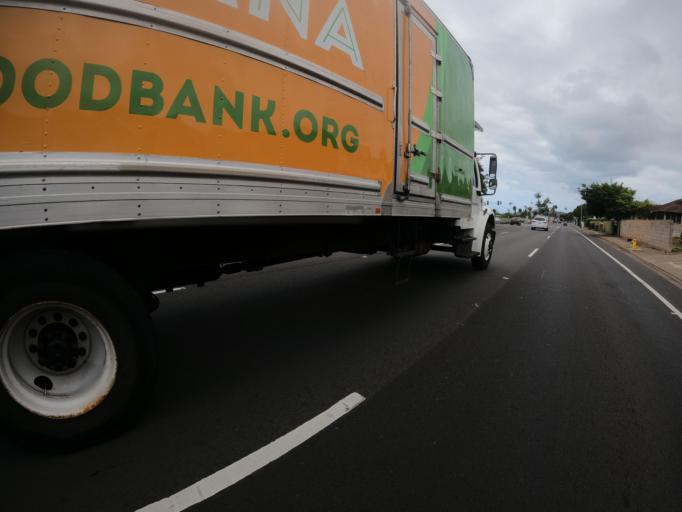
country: US
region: Hawaii
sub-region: Honolulu County
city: Waimanalo
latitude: 21.2780
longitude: -157.7565
